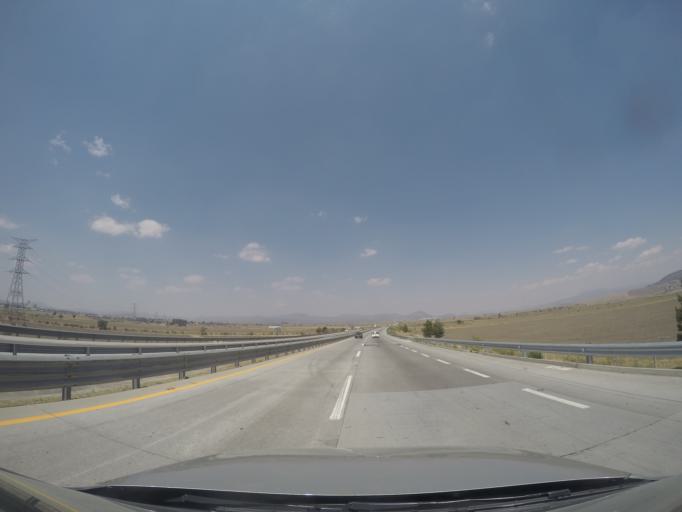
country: MX
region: Hidalgo
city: Calpulalpan
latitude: 19.5860
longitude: -98.5196
